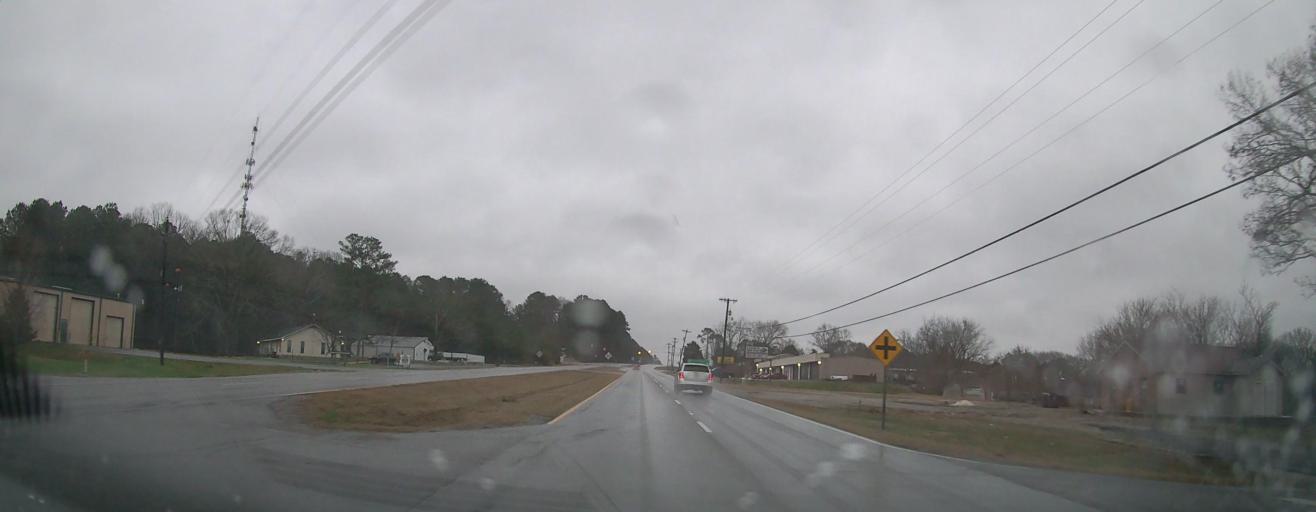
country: US
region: Alabama
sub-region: Morgan County
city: Flint City
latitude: 34.5254
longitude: -86.9713
